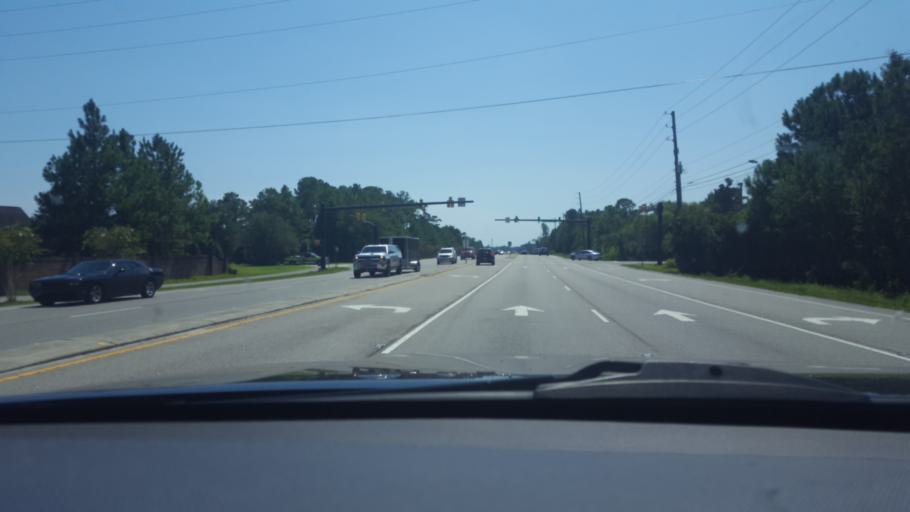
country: US
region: North Carolina
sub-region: New Hanover County
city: Ogden
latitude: 34.2504
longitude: -77.8269
